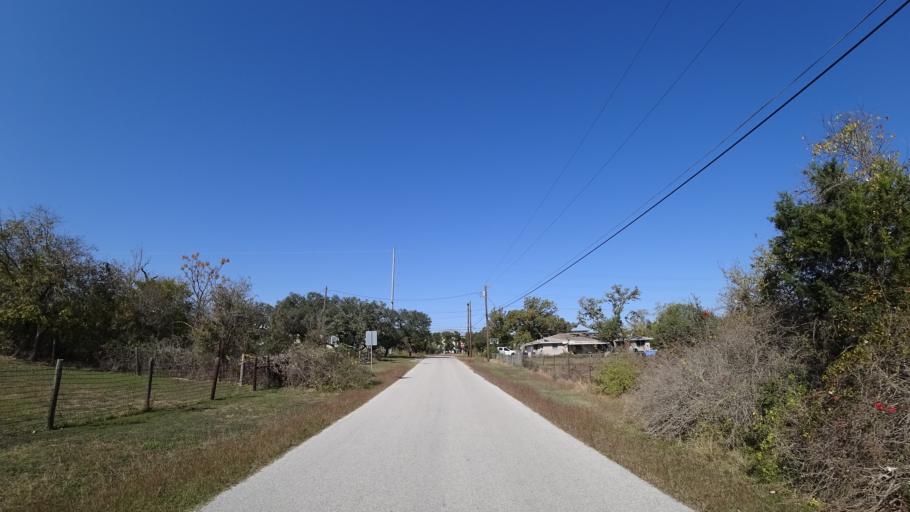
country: US
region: Texas
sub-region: Travis County
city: Barton Creek
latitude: 30.2301
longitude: -97.8584
